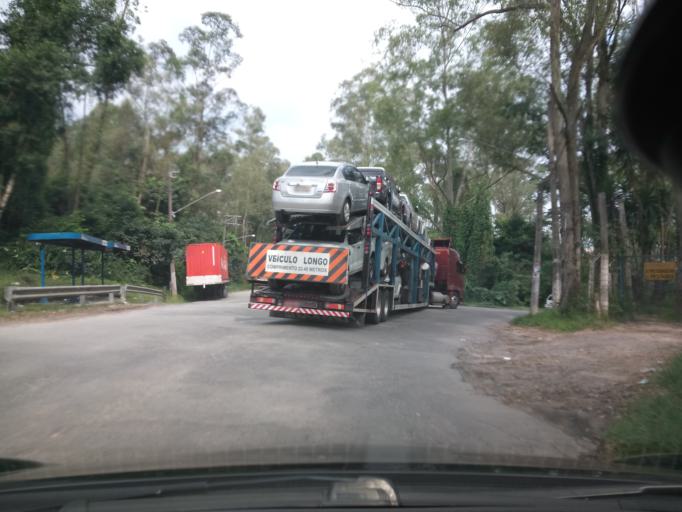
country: BR
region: Sao Paulo
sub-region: Sao Bernardo Do Campo
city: Sao Bernardo do Campo
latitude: -23.7493
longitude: -46.5931
